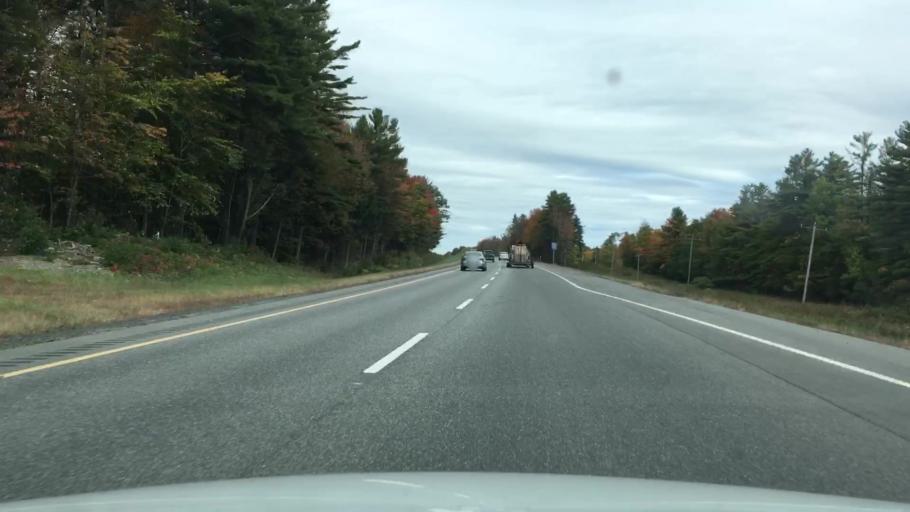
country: US
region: Maine
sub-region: Kennebec County
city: Vassalboro
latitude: 44.4565
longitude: -69.7135
